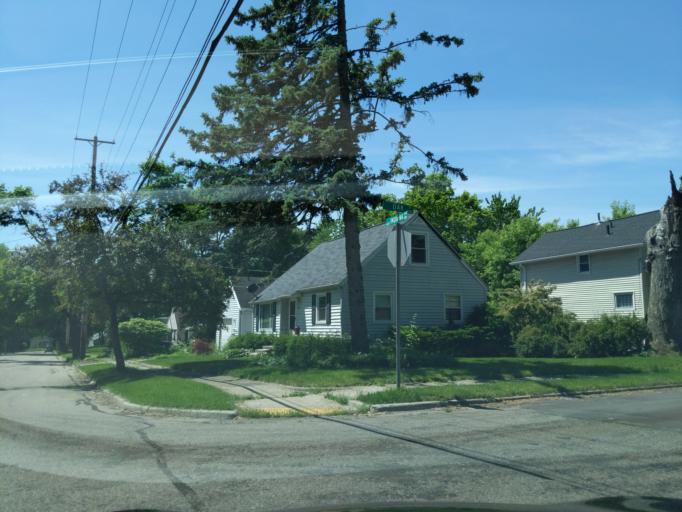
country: US
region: Michigan
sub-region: Ingham County
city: Lansing
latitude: 42.7503
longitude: -84.5310
